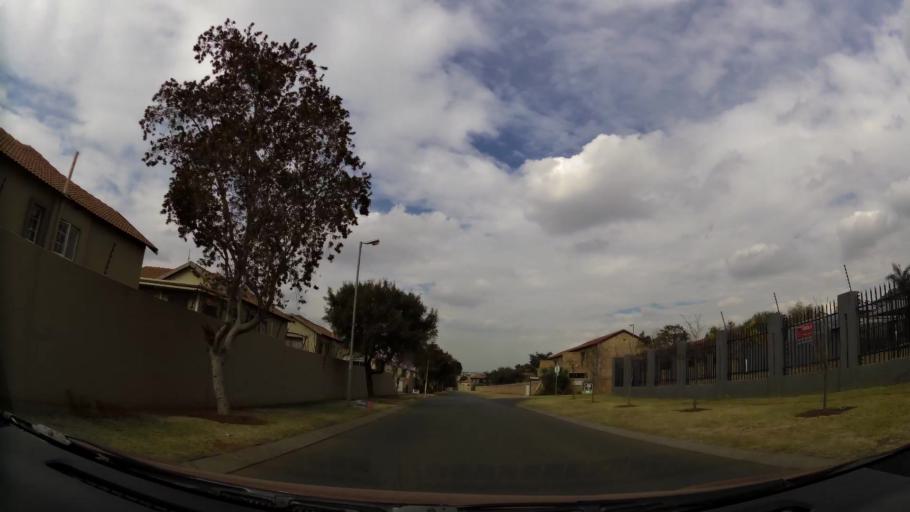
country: ZA
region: Gauteng
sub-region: City of Johannesburg Metropolitan Municipality
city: Roodepoort
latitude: -26.0974
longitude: 27.8771
